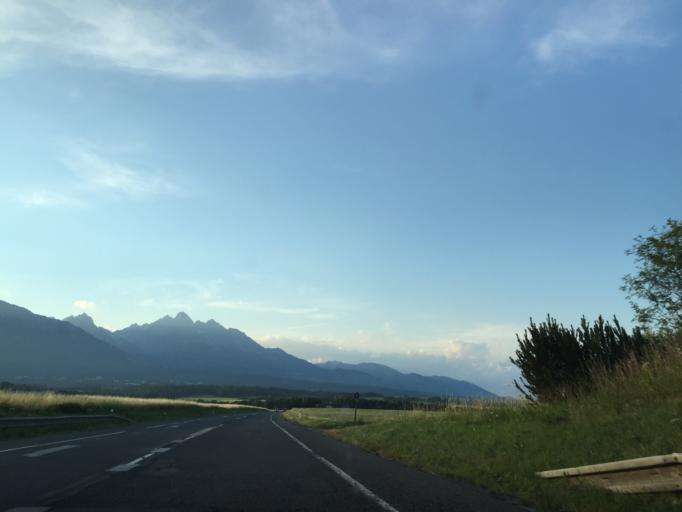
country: SK
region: Presovsky
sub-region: Okres Poprad
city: Nova Lesna
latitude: 49.0930
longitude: 20.2609
